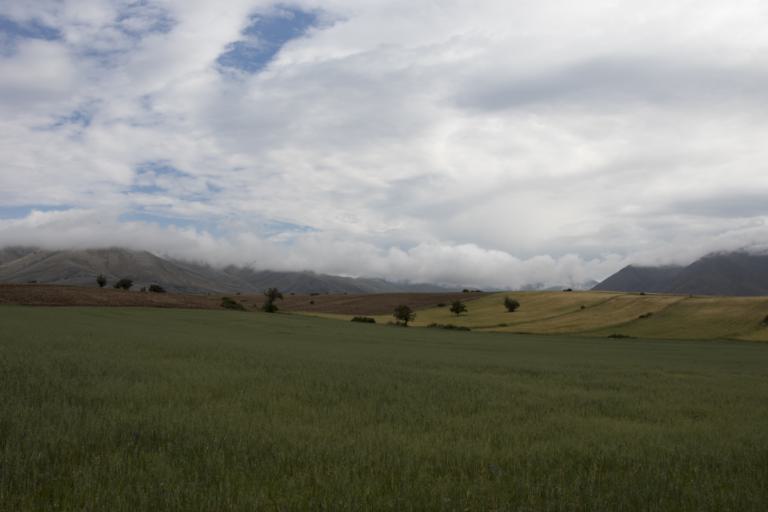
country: TR
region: Kayseri
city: Toklar
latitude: 38.4207
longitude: 36.0894
